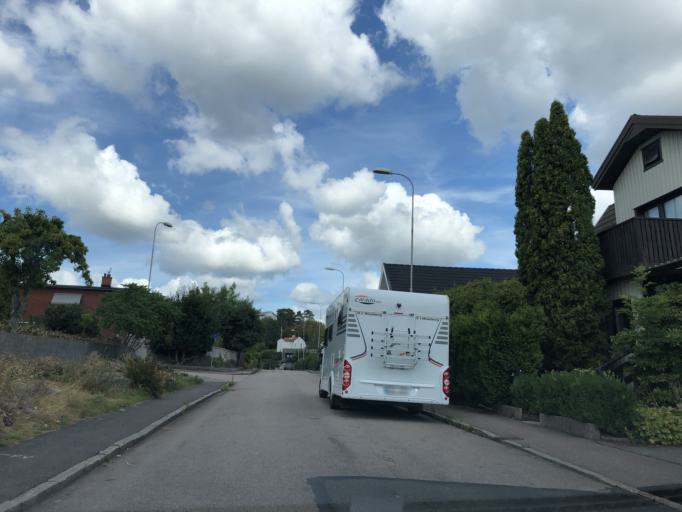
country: SE
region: Vaestra Goetaland
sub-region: Goteborg
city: Majorna
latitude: 57.7224
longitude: 11.9096
